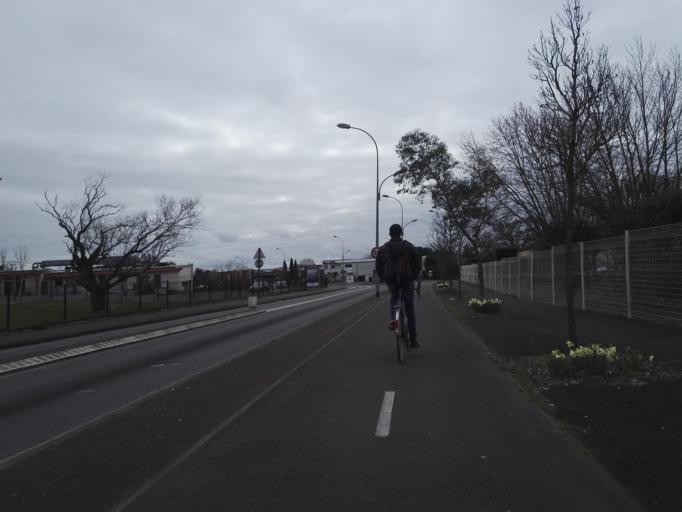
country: FR
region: Aquitaine
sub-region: Departement de la Gironde
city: Talence
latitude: 44.7879
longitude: -0.5813
